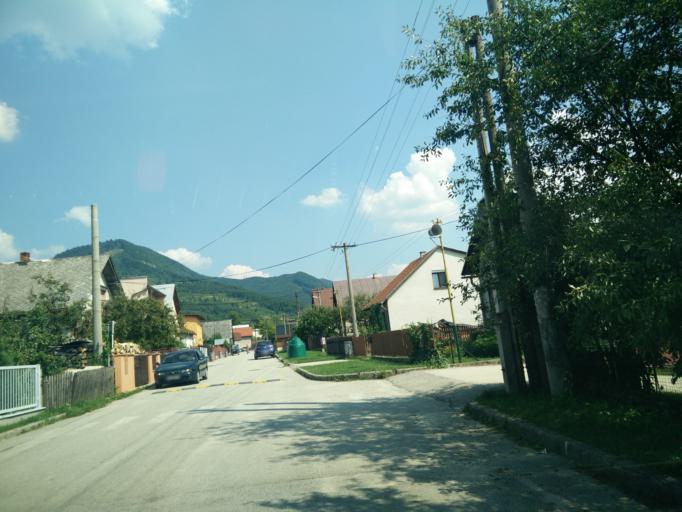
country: SK
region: Zilinsky
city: Rajec
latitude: 49.0436
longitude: 18.6353
